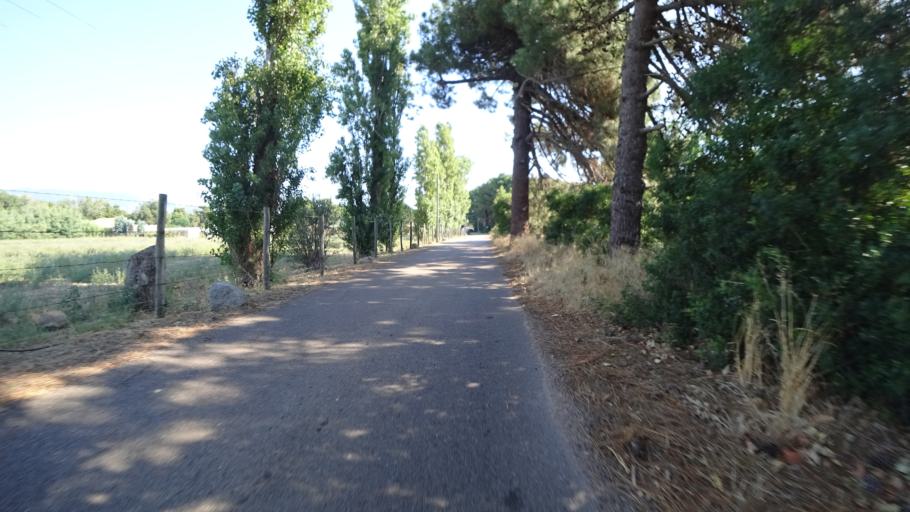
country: FR
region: Corsica
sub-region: Departement de la Corse-du-Sud
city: Porto-Vecchio
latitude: 41.6302
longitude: 9.3305
